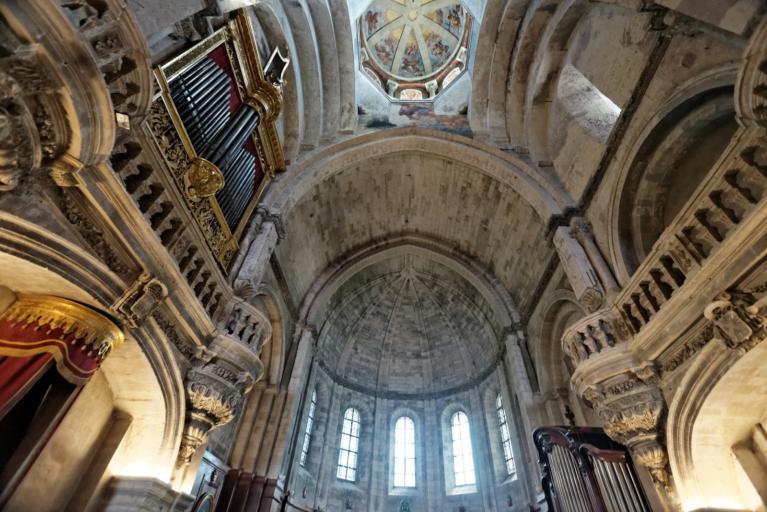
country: FR
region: Provence-Alpes-Cote d'Azur
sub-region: Departement du Vaucluse
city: Avignon
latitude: 43.9516
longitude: 4.8077
